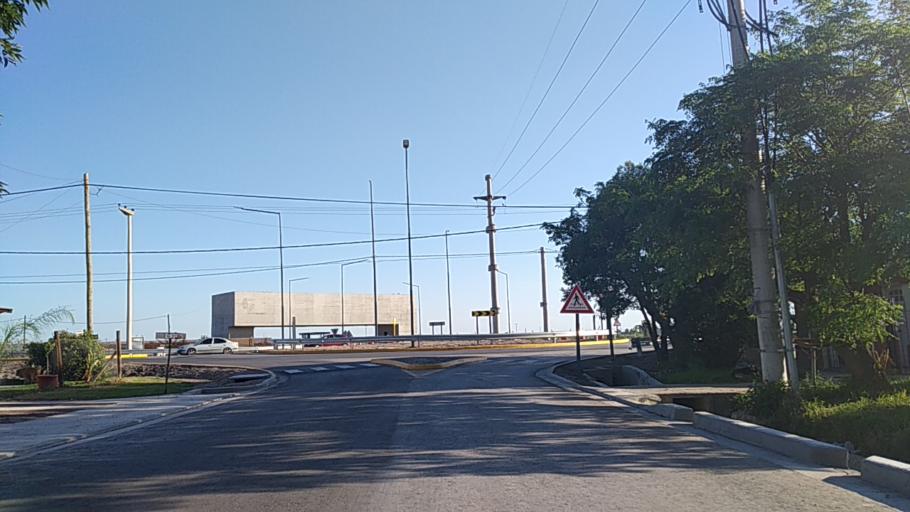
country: AR
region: Santa Fe
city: Funes
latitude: -32.9281
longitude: -60.7933
